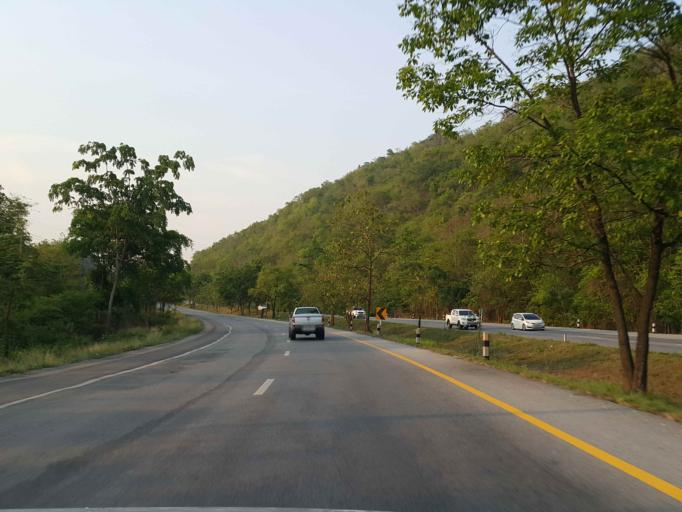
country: TH
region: Lampang
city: Sop Prap
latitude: 17.8185
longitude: 99.2826
